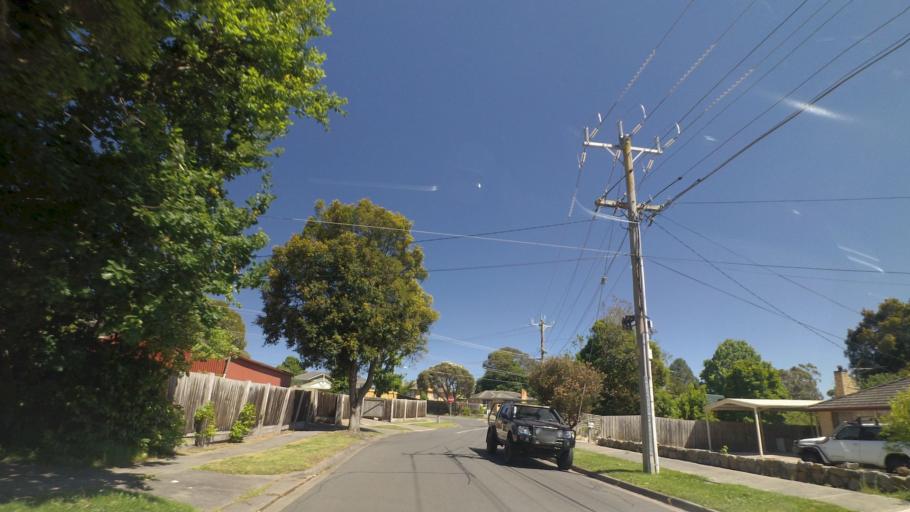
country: AU
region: Victoria
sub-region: Yarra Ranges
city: Kilsyth
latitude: -37.7924
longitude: 145.3207
